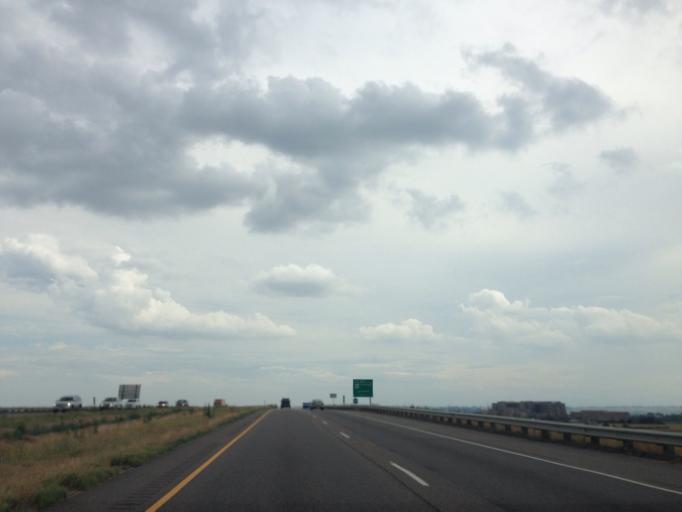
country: US
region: Colorado
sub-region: Larimer County
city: Loveland
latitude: 40.4248
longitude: -104.9929
